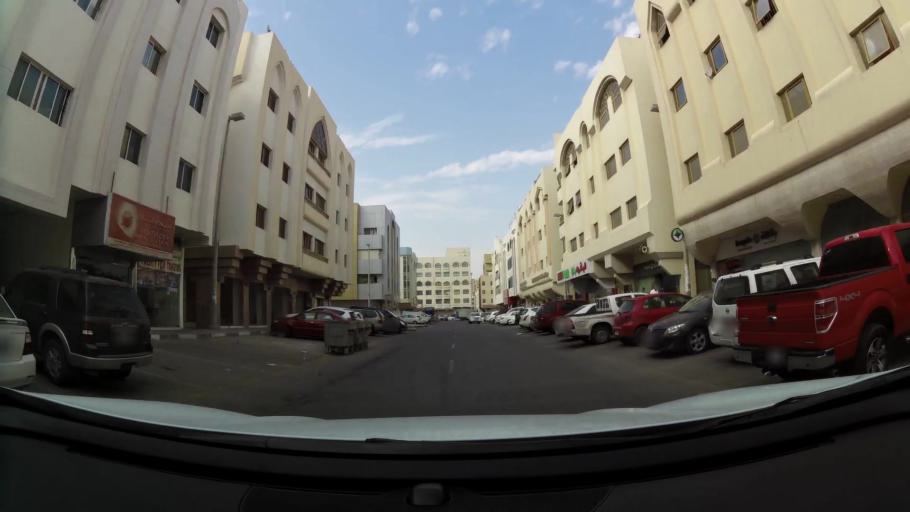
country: AE
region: Abu Dhabi
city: Abu Dhabi
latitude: 24.3233
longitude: 54.5321
